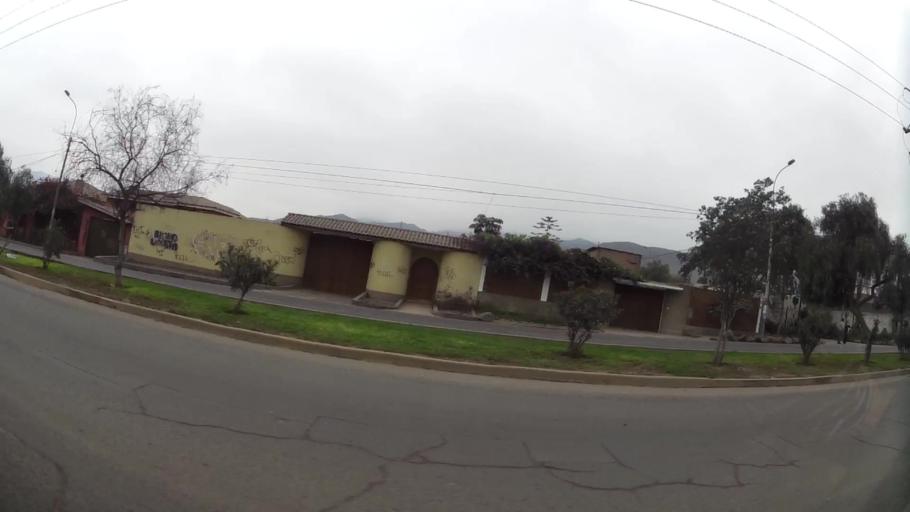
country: PE
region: Lima
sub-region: Lima
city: La Molina
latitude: -12.0862
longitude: -76.8943
